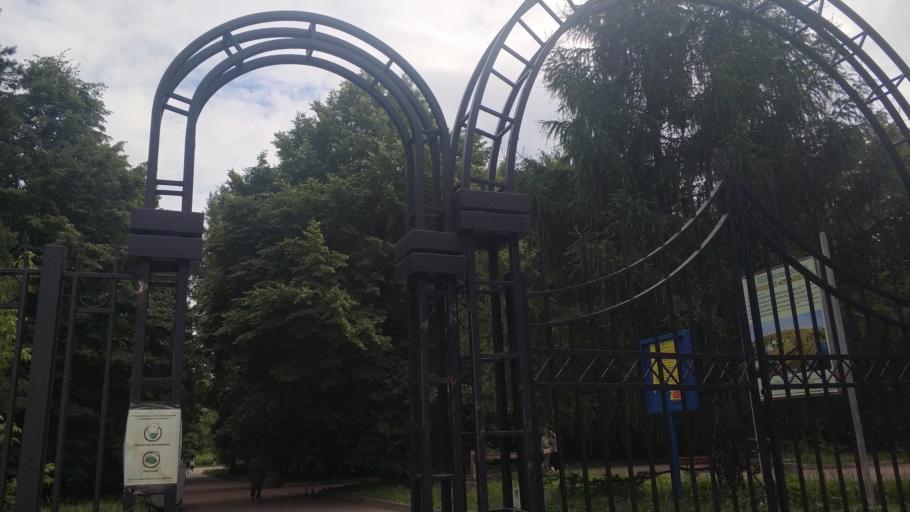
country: RU
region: Moscow
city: Perovo
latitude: 55.7388
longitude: 37.7946
